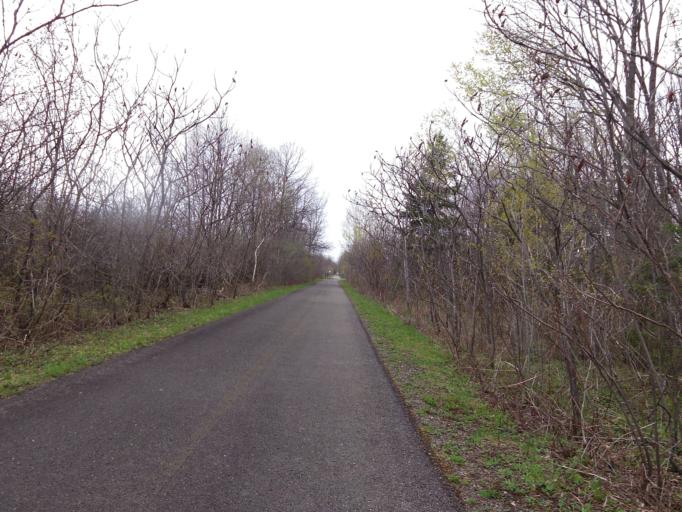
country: CA
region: Quebec
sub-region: Laurentides
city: Brownsburg-Chatham
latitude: 45.5808
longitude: -74.4121
